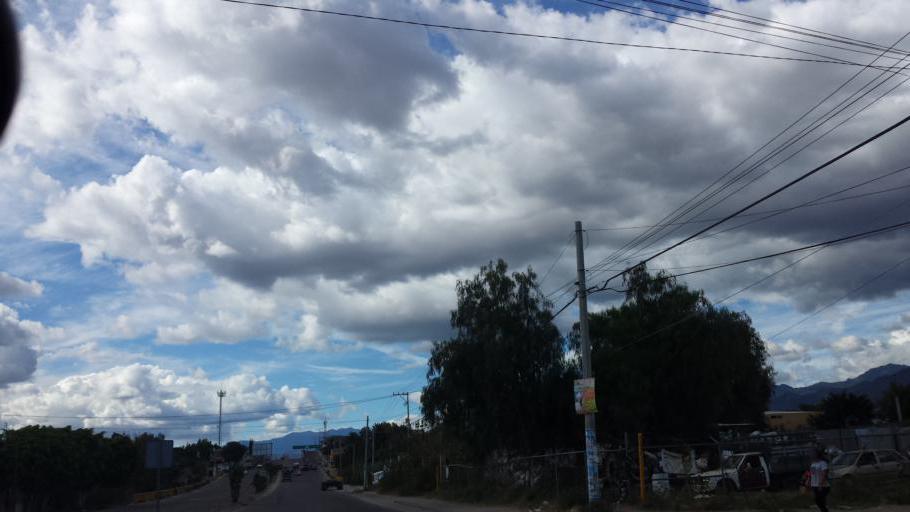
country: MX
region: Oaxaca
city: Tlacolula de Matamoros
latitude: 16.9551
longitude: -96.4707
